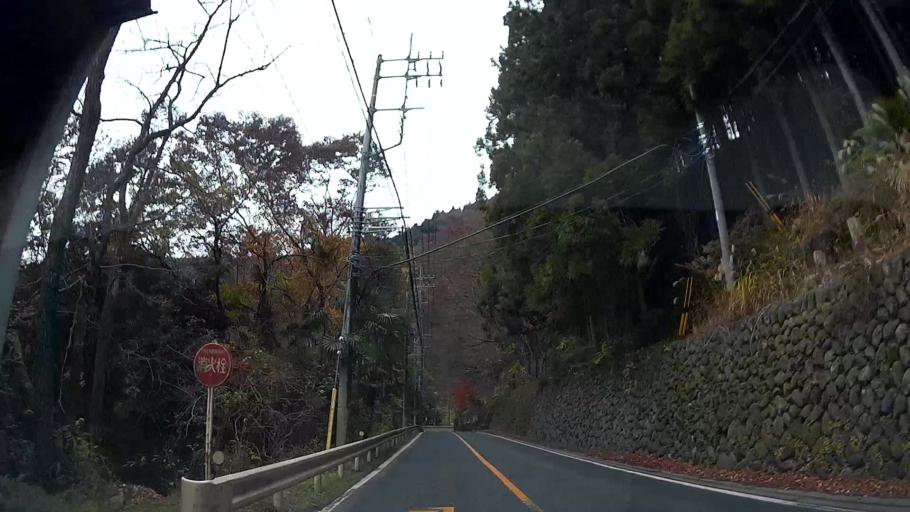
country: JP
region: Saitama
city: Chichibu
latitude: 35.9570
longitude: 138.9645
